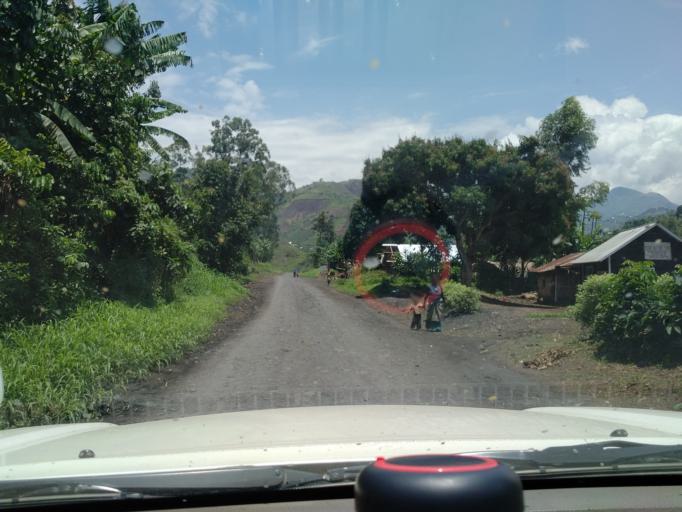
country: CD
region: Nord Kivu
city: Sake
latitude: -1.7314
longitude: 29.0078
